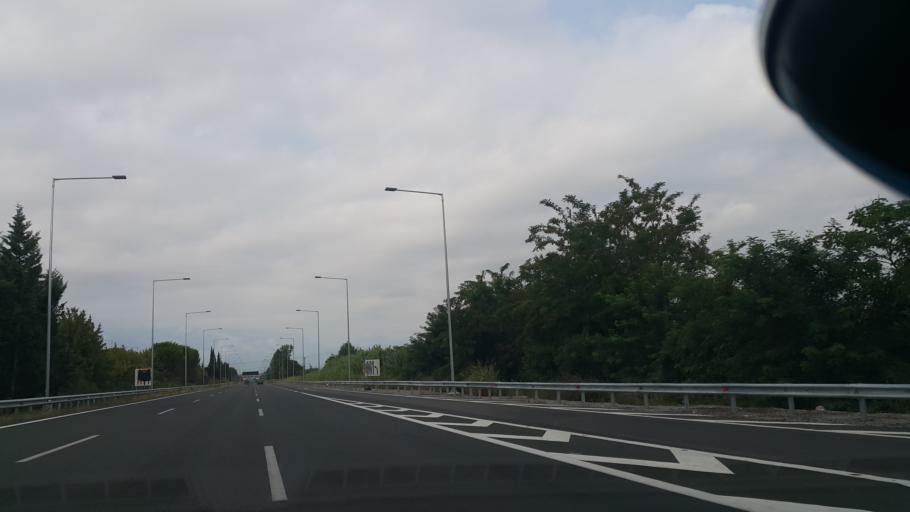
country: GR
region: Central Macedonia
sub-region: Nomos Pierias
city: Peristasi
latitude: 40.2876
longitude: 22.5315
